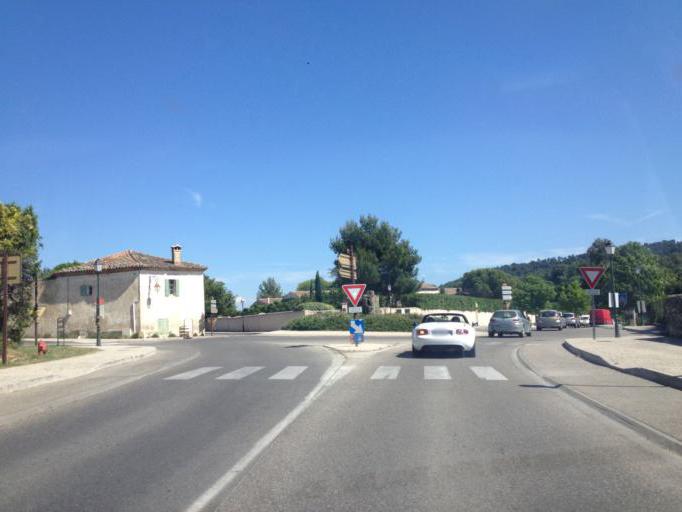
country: FR
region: Provence-Alpes-Cote d'Azur
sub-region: Departement du Vaucluse
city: Lourmarin
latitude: 43.7654
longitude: 5.3650
